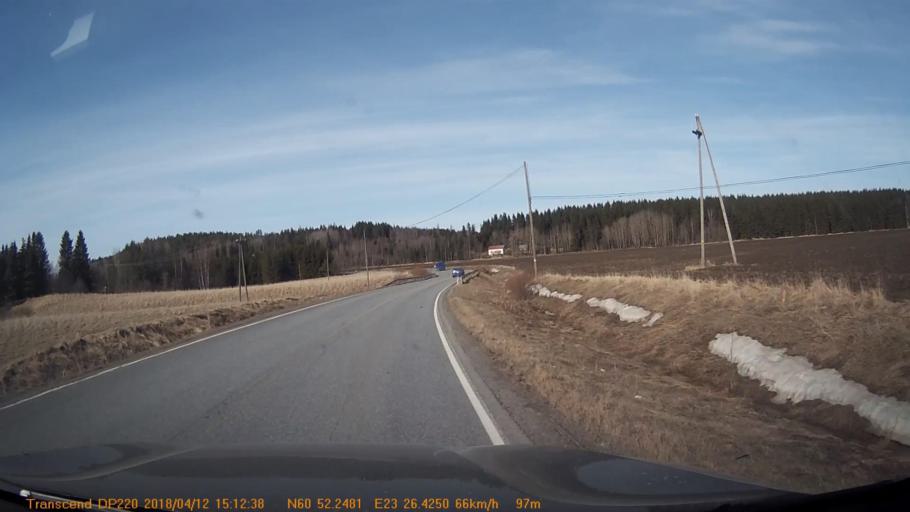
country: FI
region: Haeme
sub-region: Forssa
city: Jokioinen
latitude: 60.8709
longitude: 23.4405
